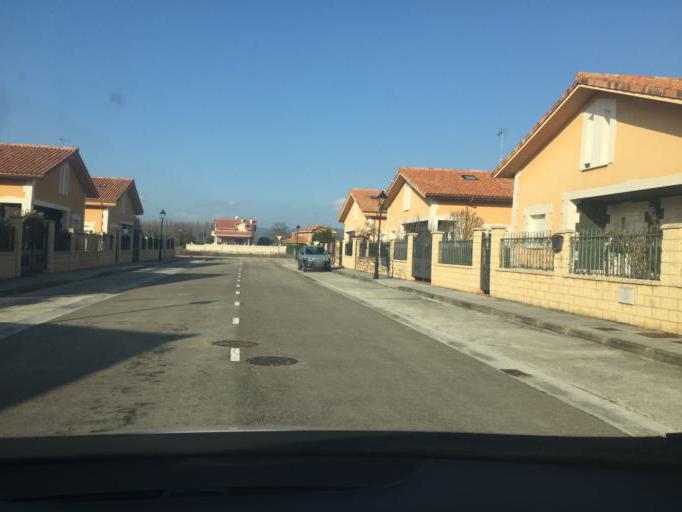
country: ES
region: Castille and Leon
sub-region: Provincia de Burgos
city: Medina de Pomar
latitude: 42.9370
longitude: -3.5830
